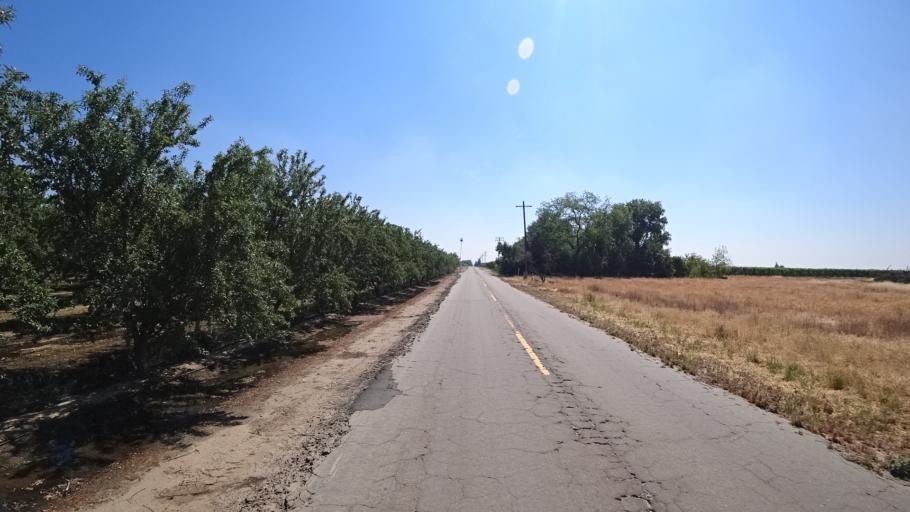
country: US
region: California
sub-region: Fresno County
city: Kingsburg
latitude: 36.4741
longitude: -119.5611
